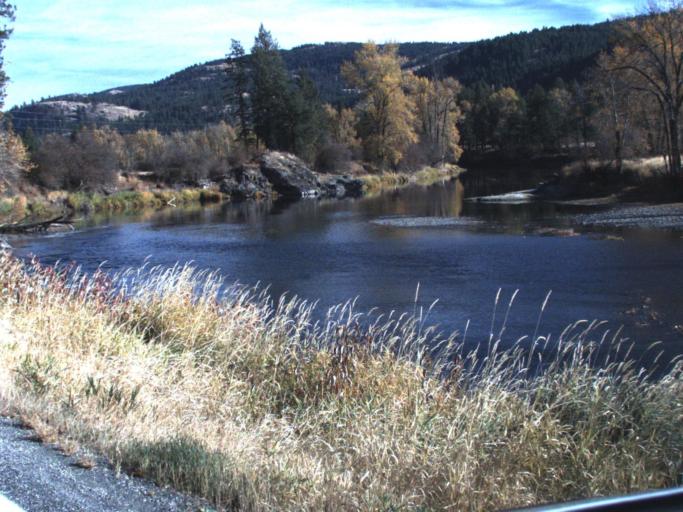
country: CA
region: British Columbia
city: Grand Forks
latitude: 48.9451
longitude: -118.5545
